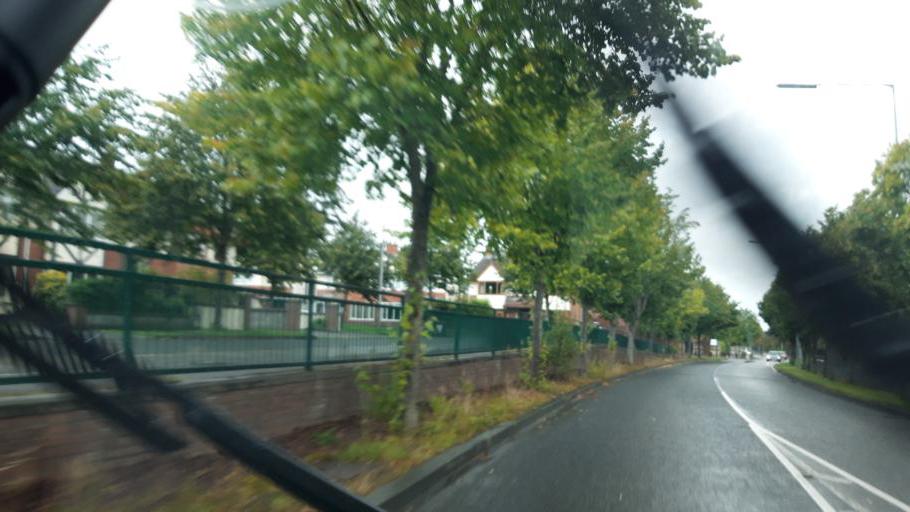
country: IE
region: Leinster
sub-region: Fingal County
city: Blanchardstown
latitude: 53.3724
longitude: -6.3990
